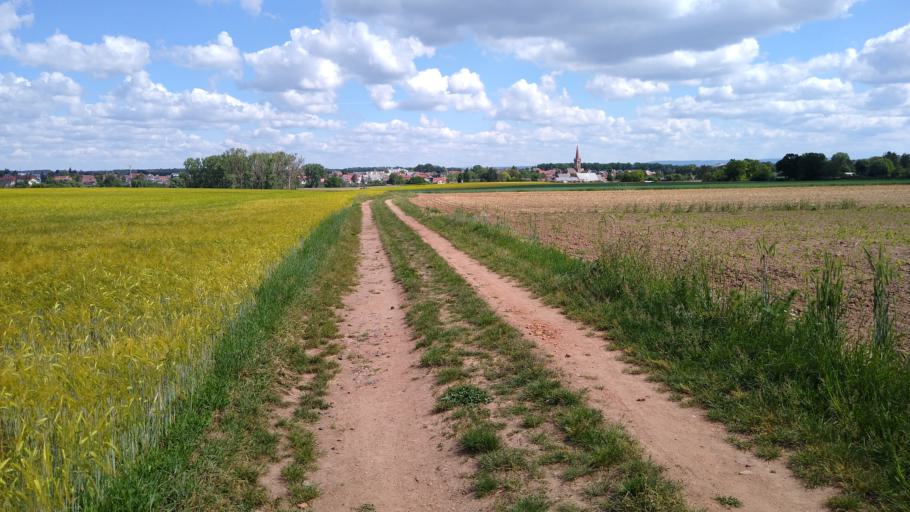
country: DE
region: Bavaria
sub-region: Regierungsbezirk Mittelfranken
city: Seukendorf
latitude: 49.4786
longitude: 10.9164
